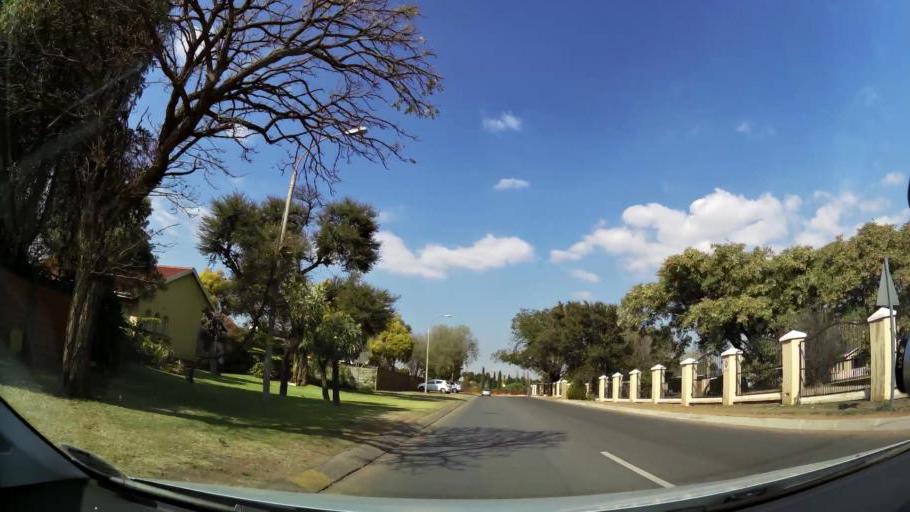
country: ZA
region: Gauteng
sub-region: City of Johannesburg Metropolitan Municipality
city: Modderfontein
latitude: -26.0836
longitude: 28.2571
